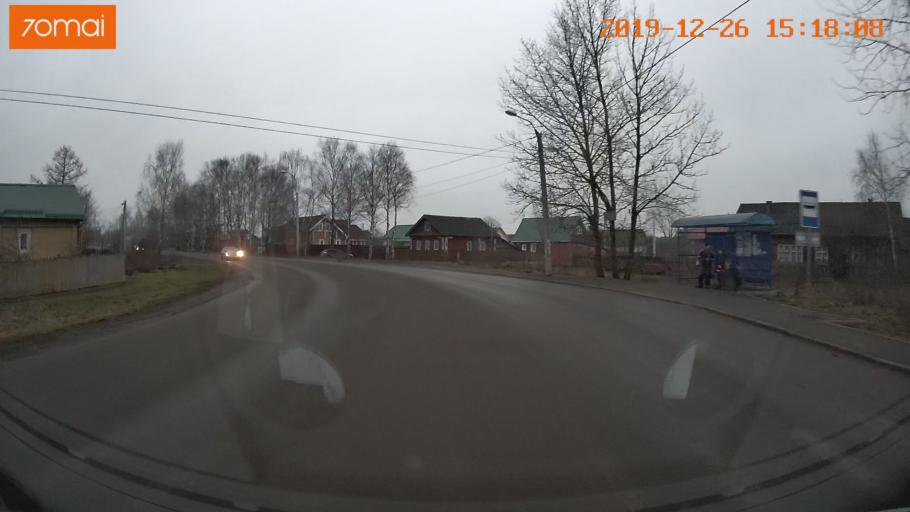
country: RU
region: Jaroslavl
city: Rybinsk
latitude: 58.0718
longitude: 38.8438
